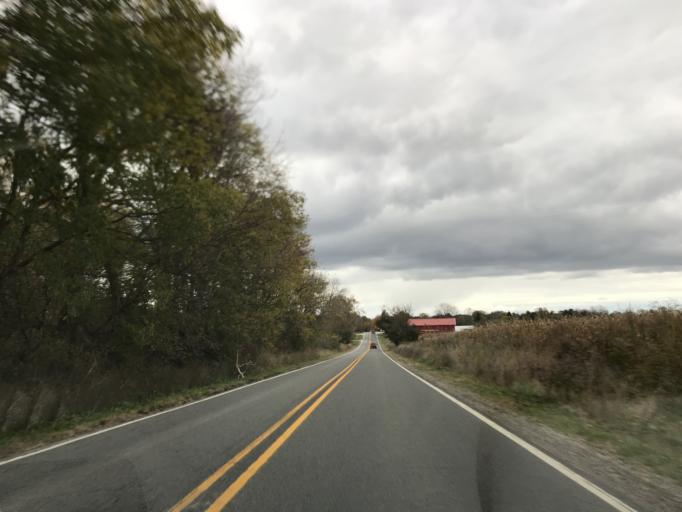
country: US
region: Michigan
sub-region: Washtenaw County
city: Ann Arbor
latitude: 42.3431
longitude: -83.7082
